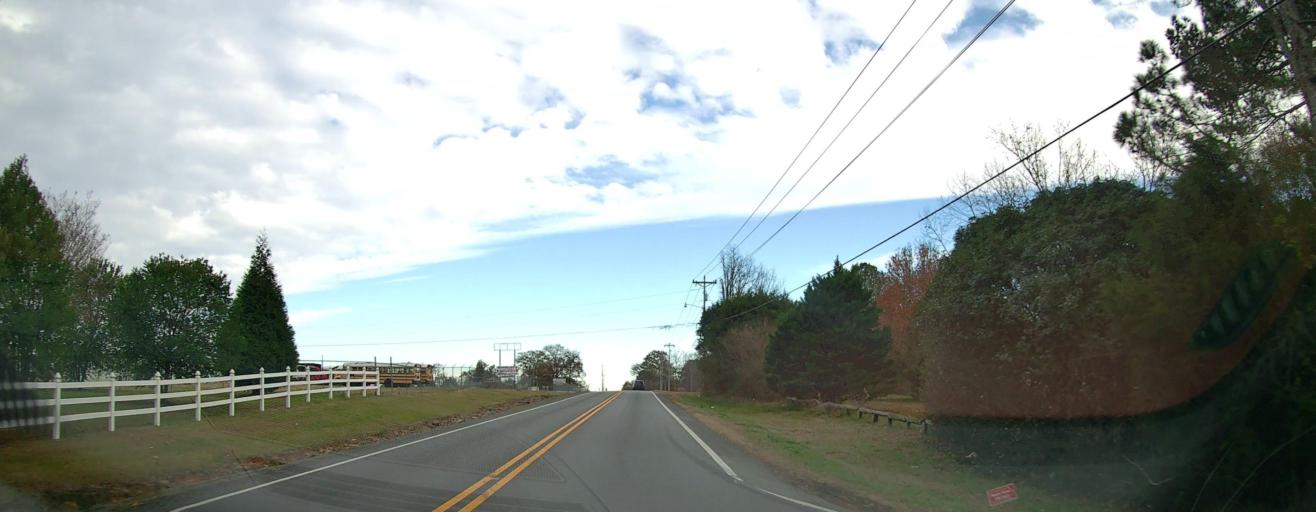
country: US
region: Alabama
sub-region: Morgan County
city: Priceville
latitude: 34.4745
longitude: -86.8082
